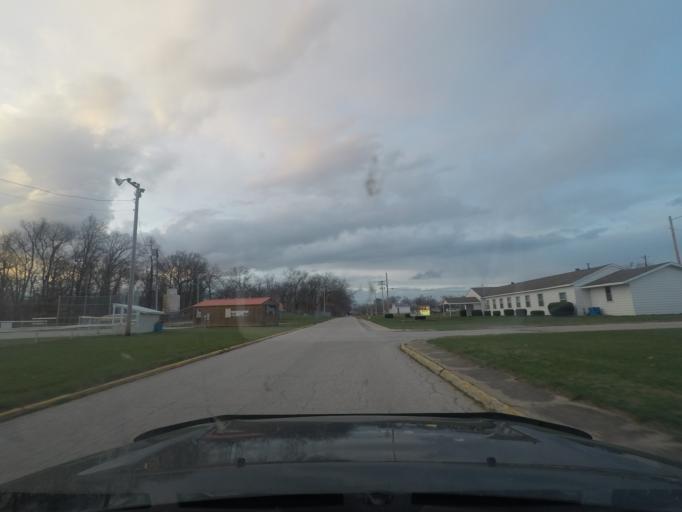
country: US
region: Indiana
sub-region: LaPorte County
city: Kingsford Heights
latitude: 41.4771
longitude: -86.6931
